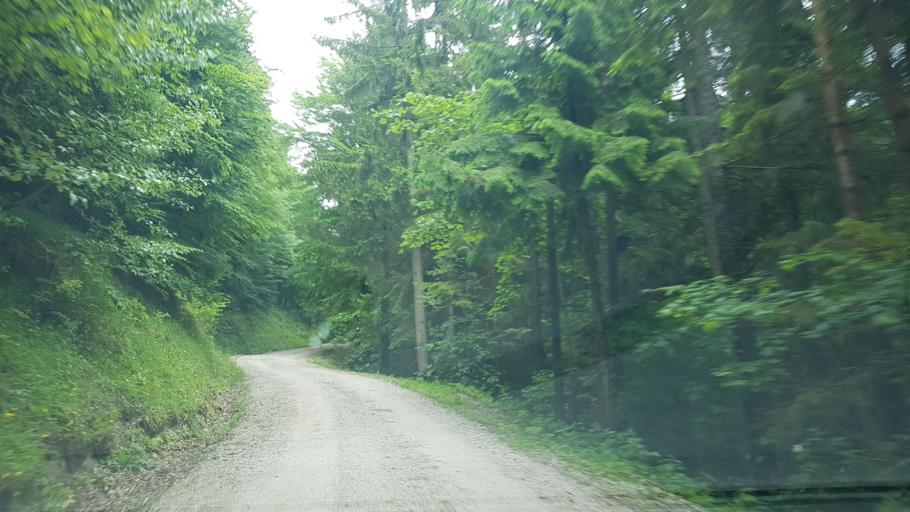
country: SI
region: Dobrna
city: Dobrna
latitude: 46.3848
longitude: 15.2166
